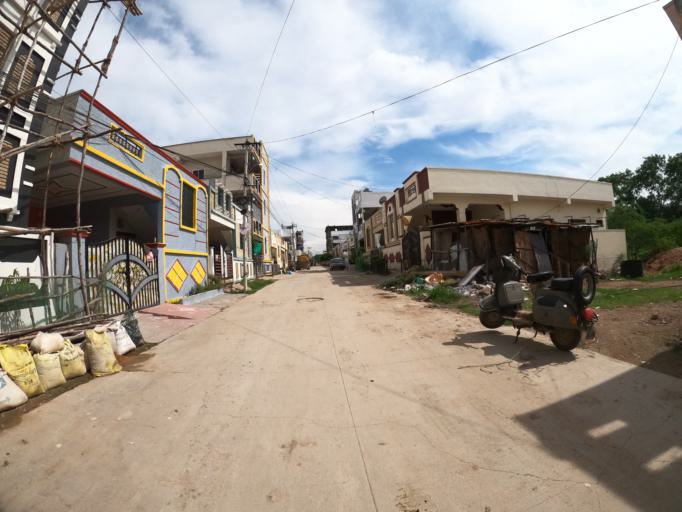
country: IN
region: Telangana
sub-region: Hyderabad
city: Hyderabad
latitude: 17.3647
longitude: 78.3835
